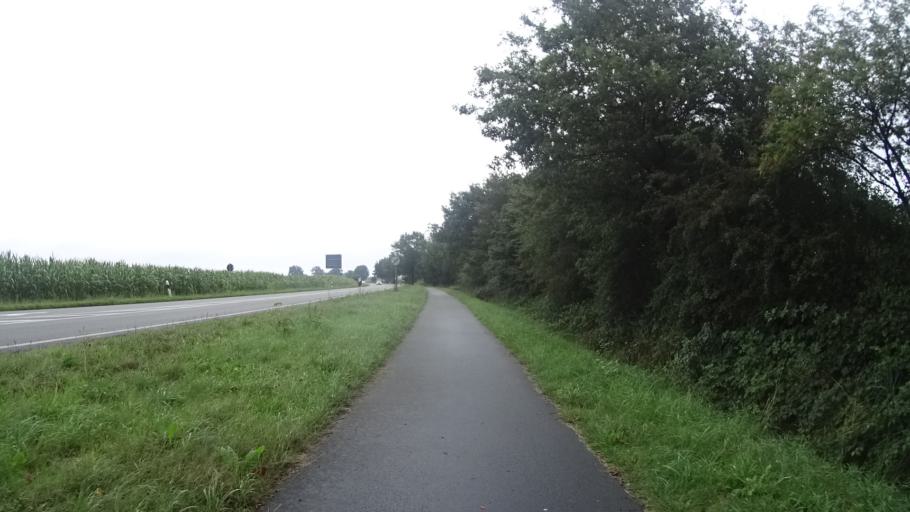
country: DE
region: Lower Saxony
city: Brinkum
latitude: 53.2714
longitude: 7.5581
